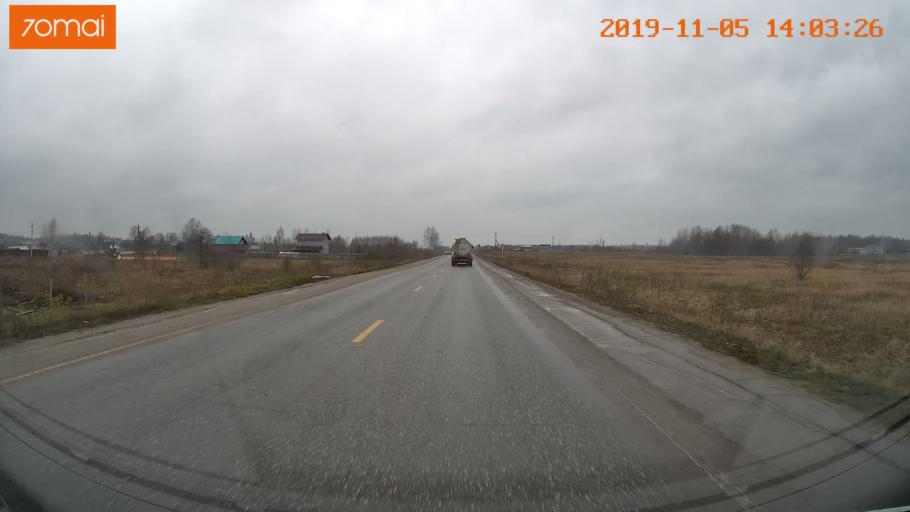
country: RU
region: Ivanovo
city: Kokhma
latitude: 56.9984
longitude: 41.1960
